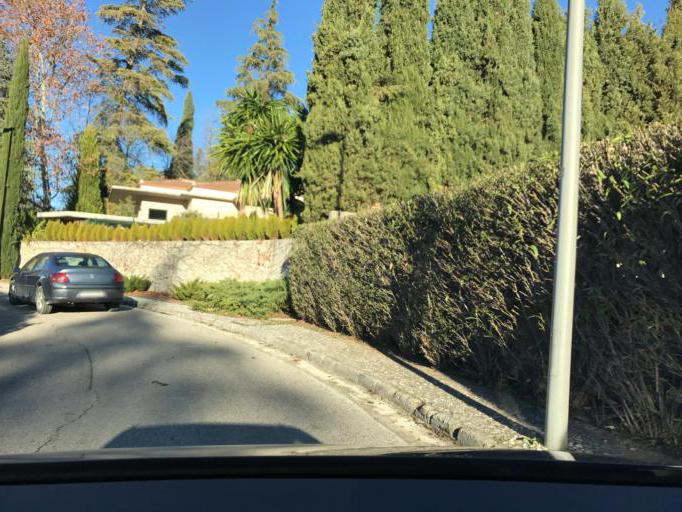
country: ES
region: Andalusia
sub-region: Provincia de Granada
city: Albolote
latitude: 37.2515
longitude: -3.6512
